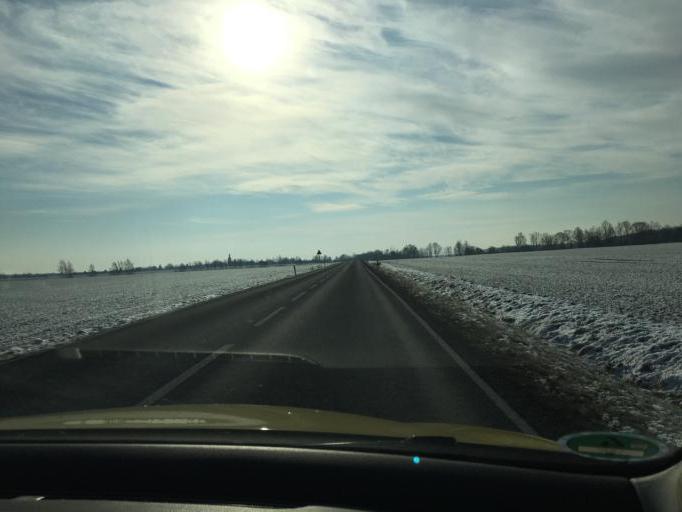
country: DE
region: Saxony
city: Otterwisch
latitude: 51.1856
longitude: 12.6152
